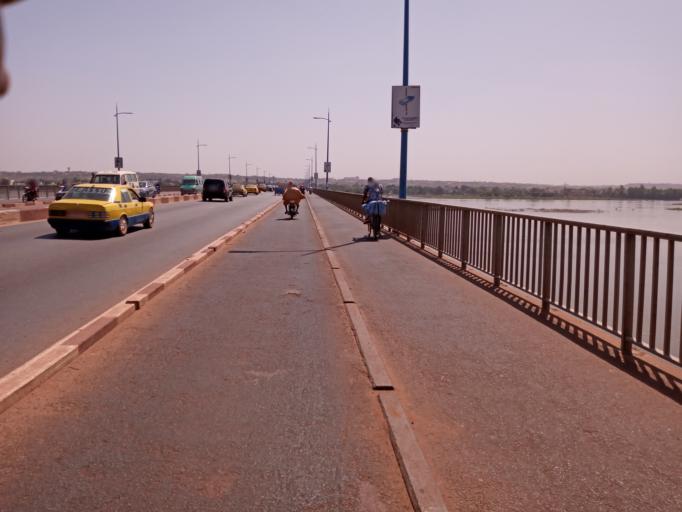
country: ML
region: Bamako
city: Bamako
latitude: 12.6261
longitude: -8.0067
